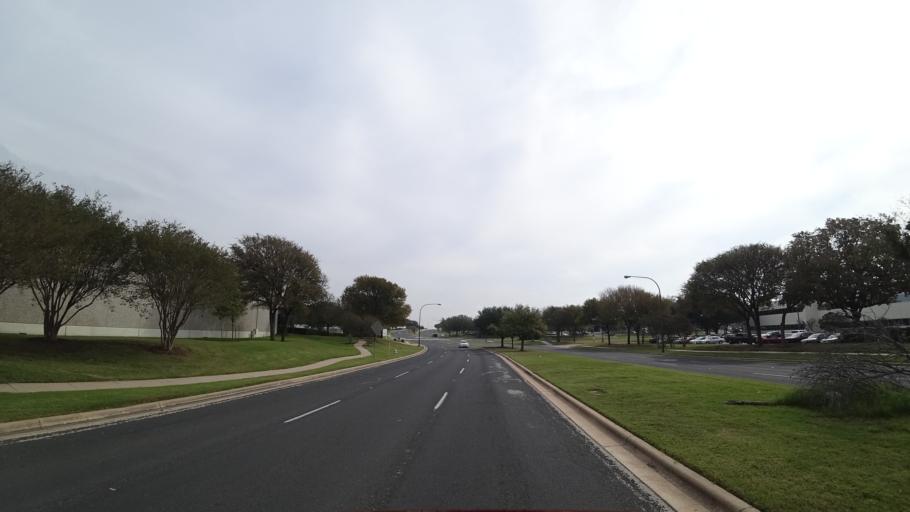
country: US
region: Texas
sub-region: Travis County
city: Wells Branch
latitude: 30.4569
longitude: -97.6734
